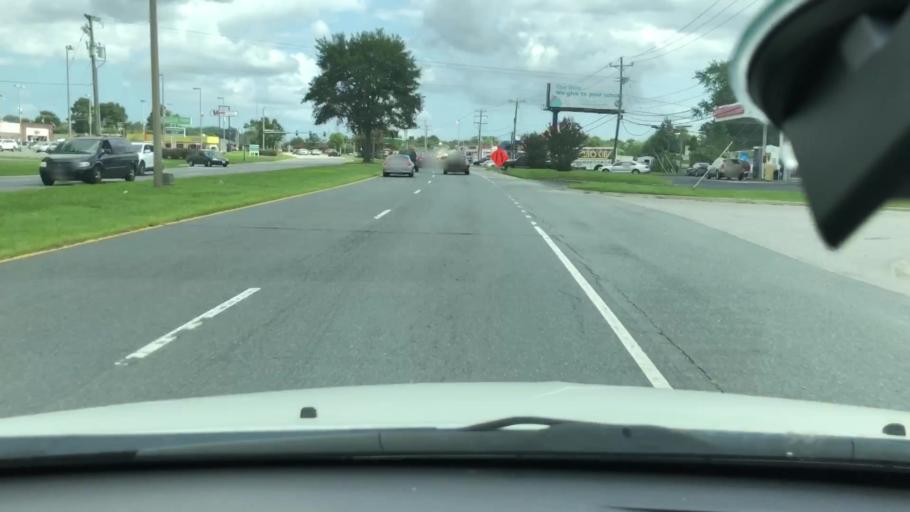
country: US
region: Virginia
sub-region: City of Chesapeake
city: Chesapeake
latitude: 36.8076
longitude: -76.2205
